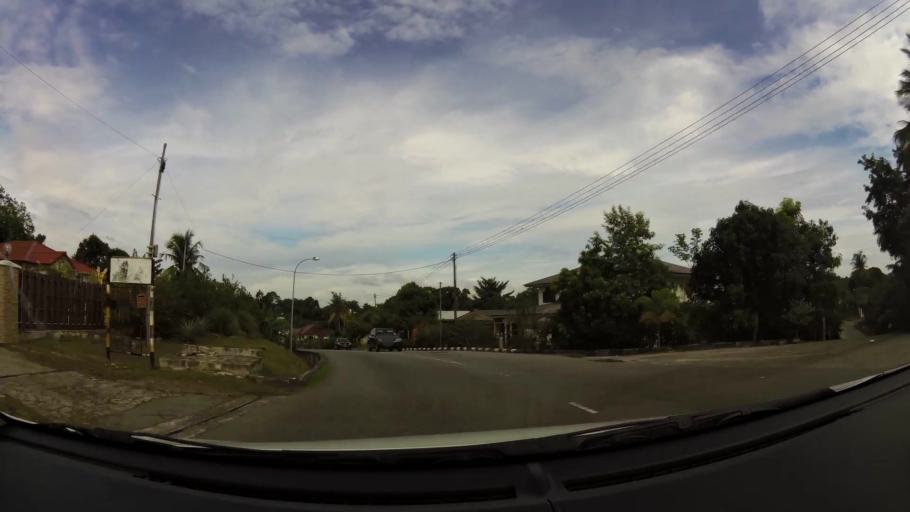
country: BN
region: Brunei and Muara
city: Bandar Seri Begawan
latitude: 4.9003
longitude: 114.8922
